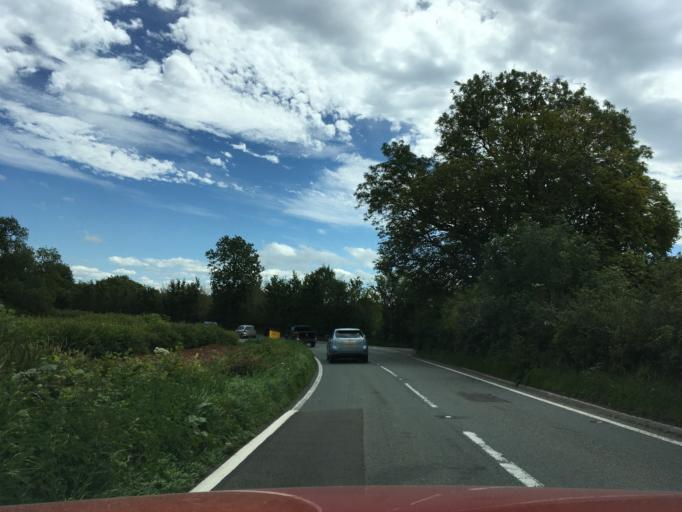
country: GB
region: England
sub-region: Somerset
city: Wells
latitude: 51.2165
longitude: -2.6893
